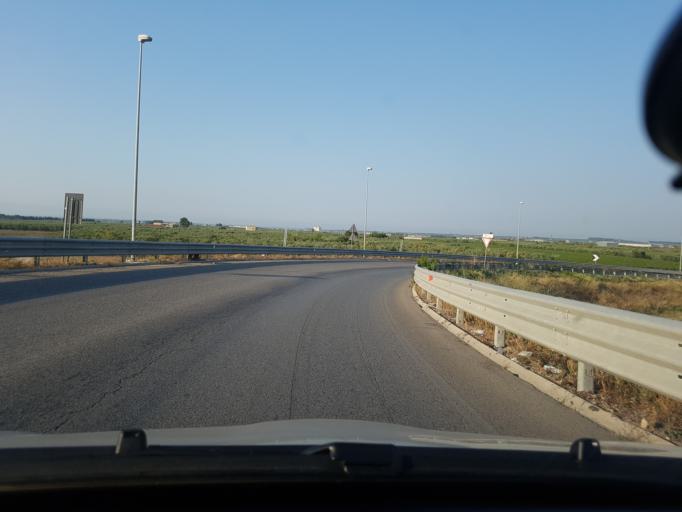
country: IT
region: Apulia
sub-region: Provincia di Foggia
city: Cerignola
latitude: 41.2759
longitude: 15.8751
